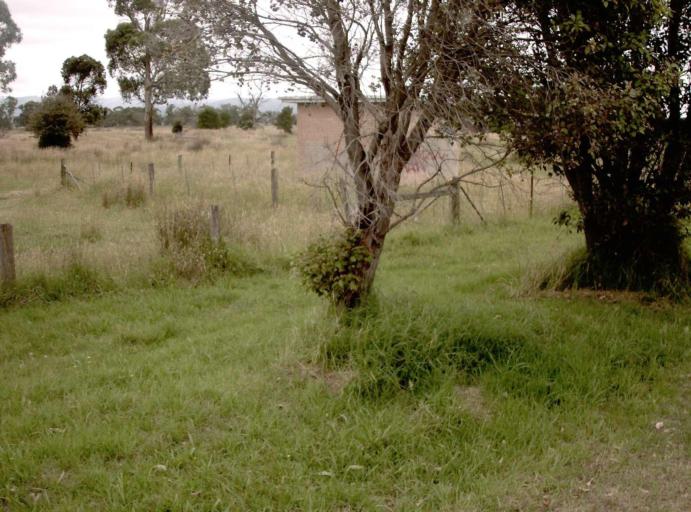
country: AU
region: Victoria
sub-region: Cardinia
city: Bunyip
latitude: -38.1097
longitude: 145.7744
